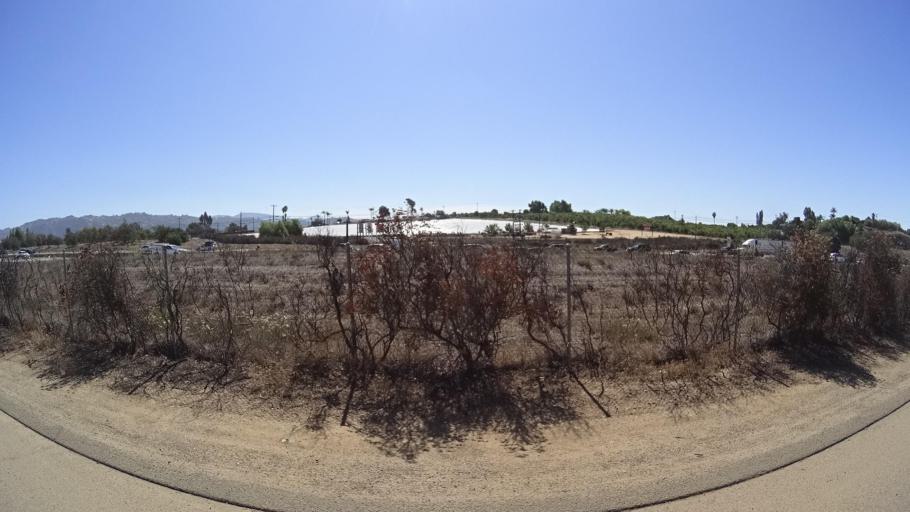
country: US
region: California
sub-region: San Diego County
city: Rainbow
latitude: 33.4034
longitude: -117.1684
